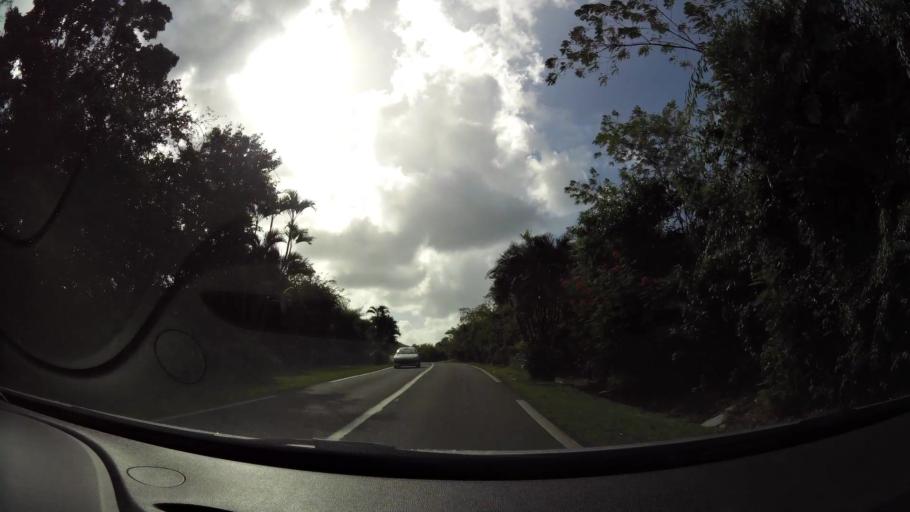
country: MQ
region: Martinique
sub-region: Martinique
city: Les Trois-Ilets
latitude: 14.5375
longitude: -61.0461
